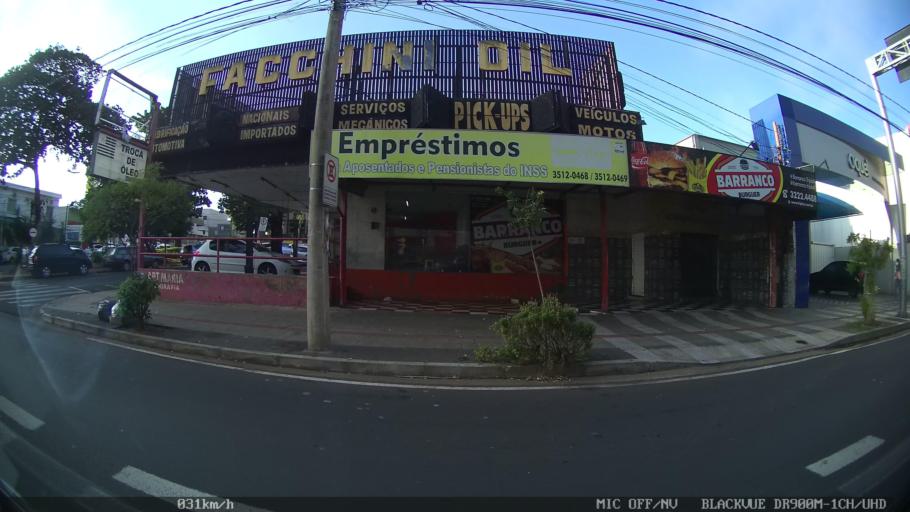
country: BR
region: Sao Paulo
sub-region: Sao Jose Do Rio Preto
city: Sao Jose do Rio Preto
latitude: -20.8144
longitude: -49.3783
